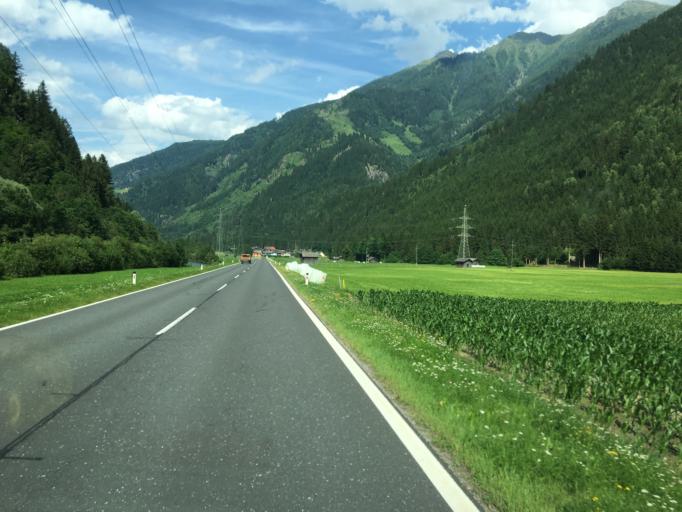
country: AT
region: Carinthia
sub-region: Politischer Bezirk Spittal an der Drau
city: Stall
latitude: 46.8907
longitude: 13.0516
